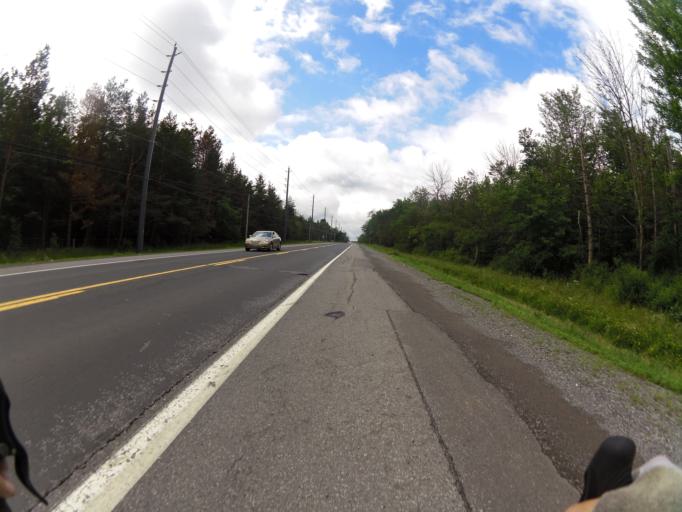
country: CA
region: Ontario
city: Bells Corners
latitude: 45.2933
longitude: -75.8353
